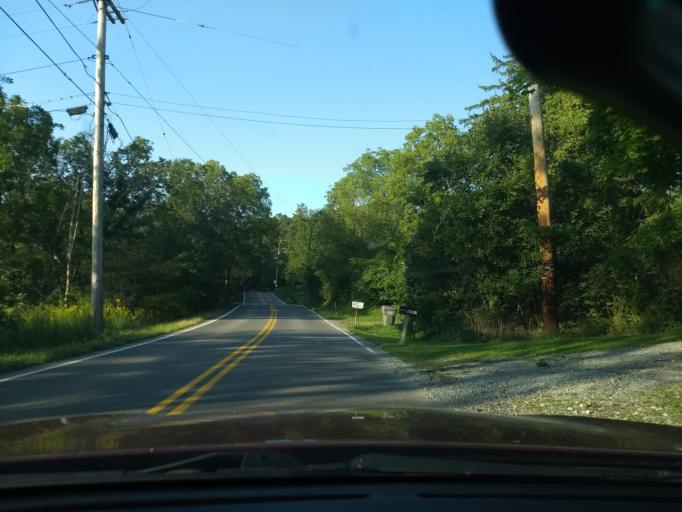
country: US
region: Pennsylvania
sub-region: Allegheny County
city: Gibsonia
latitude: 40.6333
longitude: -79.9642
